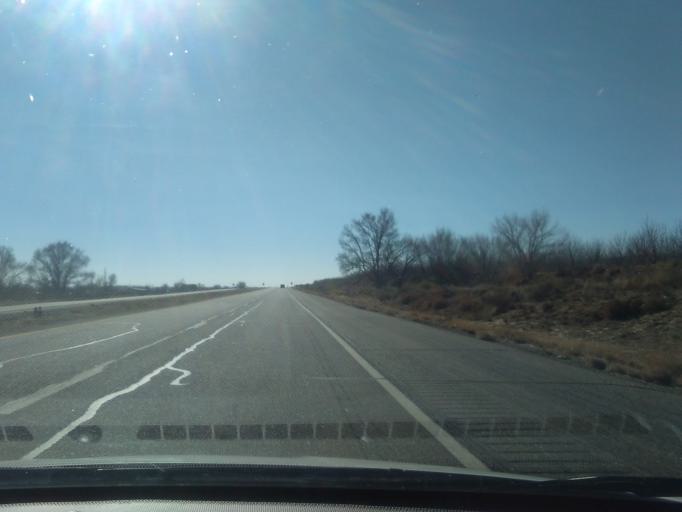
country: US
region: New Mexico
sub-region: Valencia County
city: Jarales
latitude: 34.5829
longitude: -106.7911
